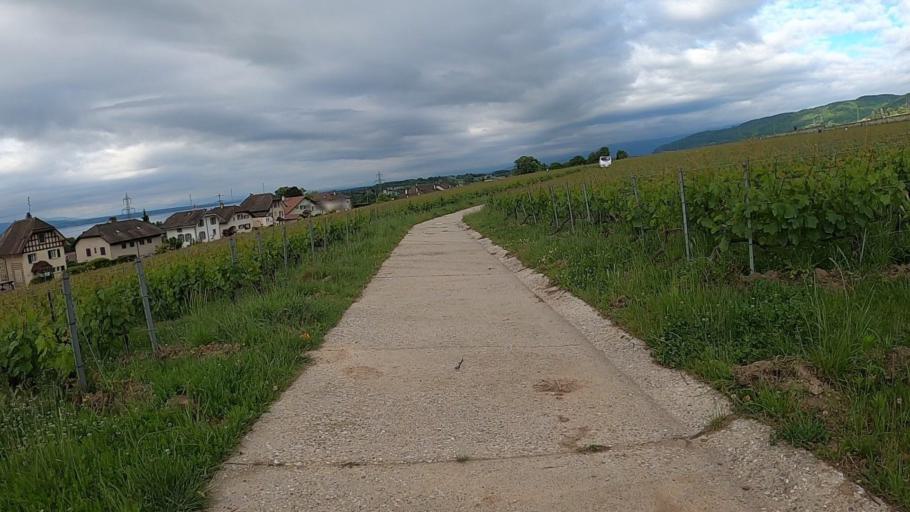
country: CH
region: Vaud
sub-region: Nyon District
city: Rolle
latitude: 46.4695
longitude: 6.3394
